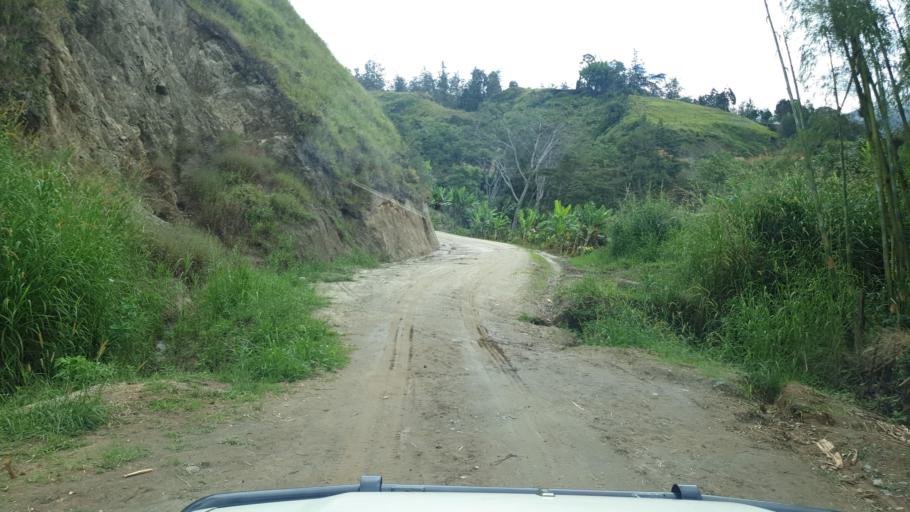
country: PG
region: Eastern Highlands
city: Goroka
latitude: -5.9274
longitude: 145.2634
